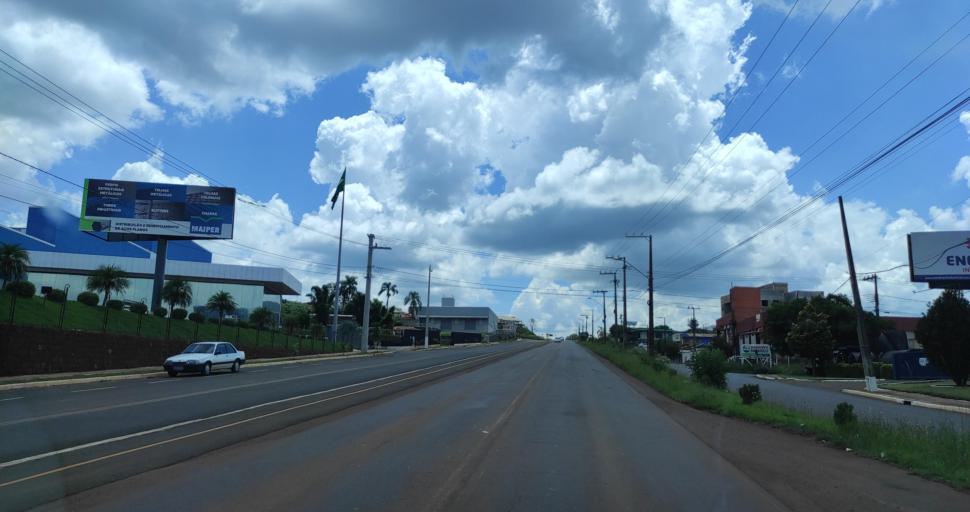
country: BR
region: Santa Catarina
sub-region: Xanxere
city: Xanxere
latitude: -26.8600
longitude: -52.4059
